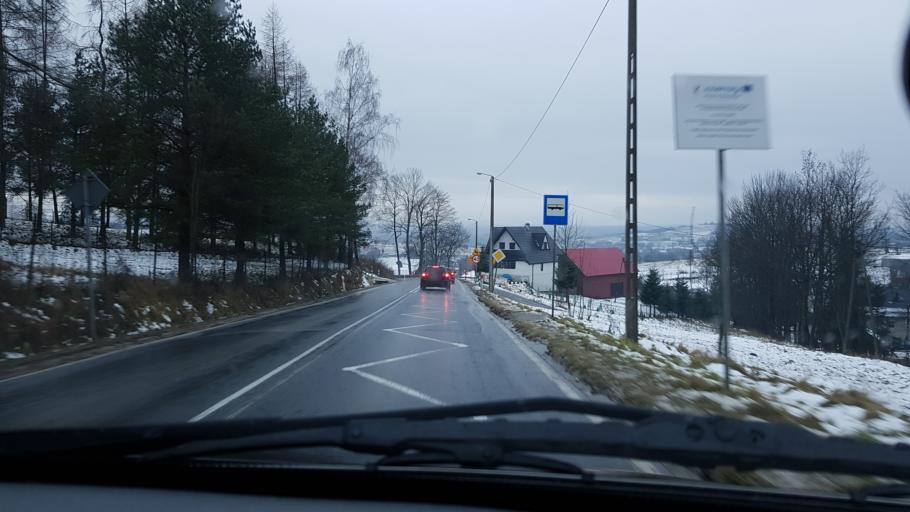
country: PL
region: Lesser Poland Voivodeship
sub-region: Powiat nowotarski
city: Sieniawa
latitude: 49.5113
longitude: 19.8906
